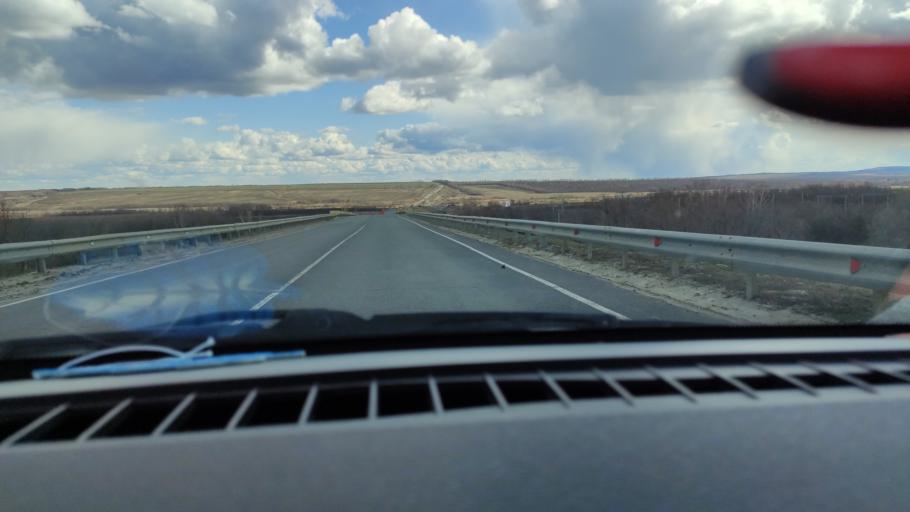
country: RU
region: Saratov
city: Dukhovnitskoye
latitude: 52.7483
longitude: 48.2502
